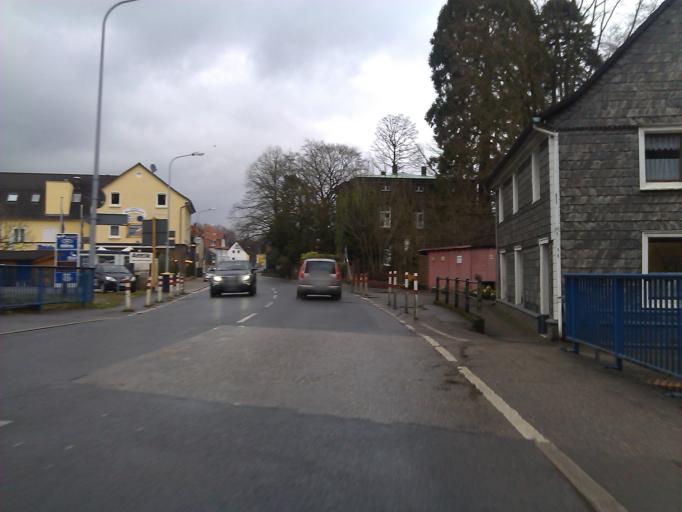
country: DE
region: North Rhine-Westphalia
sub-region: Regierungsbezirk Dusseldorf
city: Heiligenhaus
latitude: 51.3564
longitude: 6.9306
